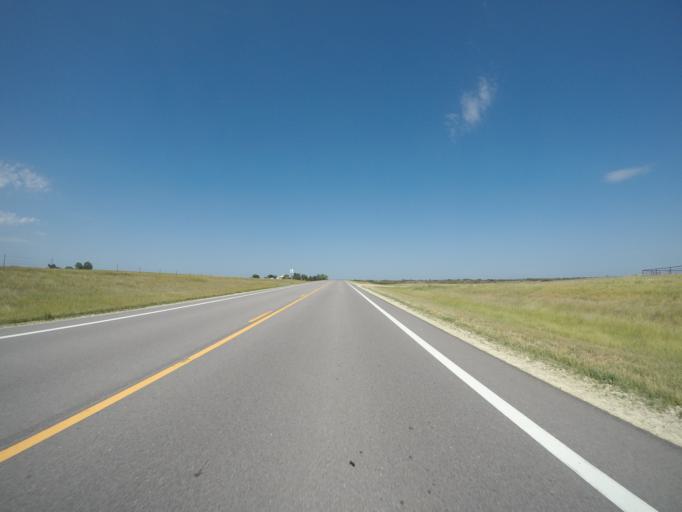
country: US
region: Kansas
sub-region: Clay County
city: Clay Center
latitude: 39.3785
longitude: -97.3471
